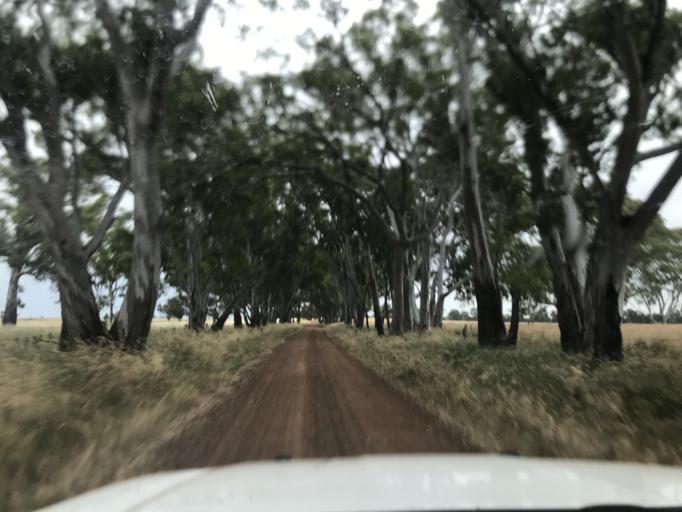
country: AU
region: Victoria
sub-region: Horsham
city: Horsham
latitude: -37.0668
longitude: 141.6739
